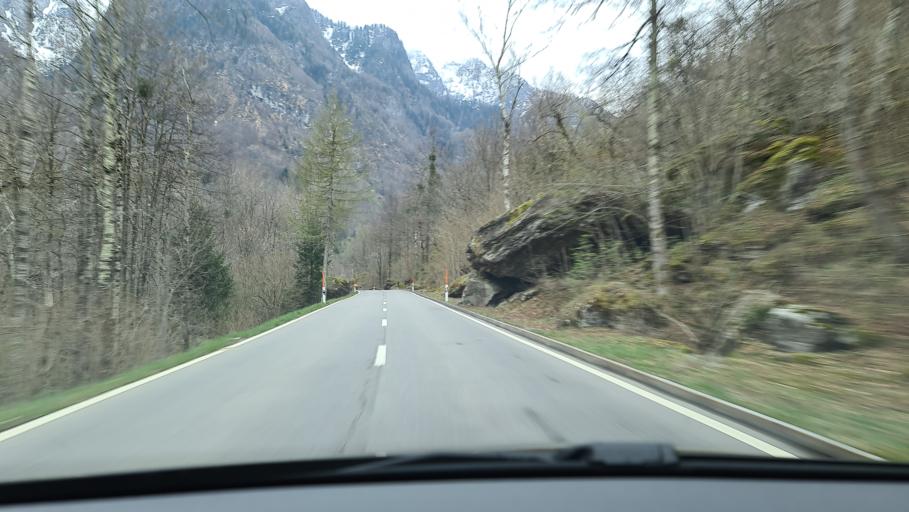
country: CH
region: Ticino
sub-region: Vallemaggia District
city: Cevio
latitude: 46.3881
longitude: 8.6618
